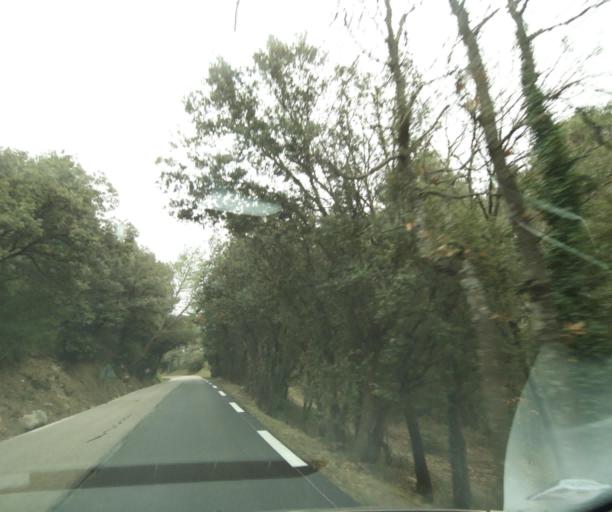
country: FR
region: Provence-Alpes-Cote d'Azur
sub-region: Departement des Bouches-du-Rhone
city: Chateauneuf-le-Rouge
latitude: 43.5546
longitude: 5.5864
